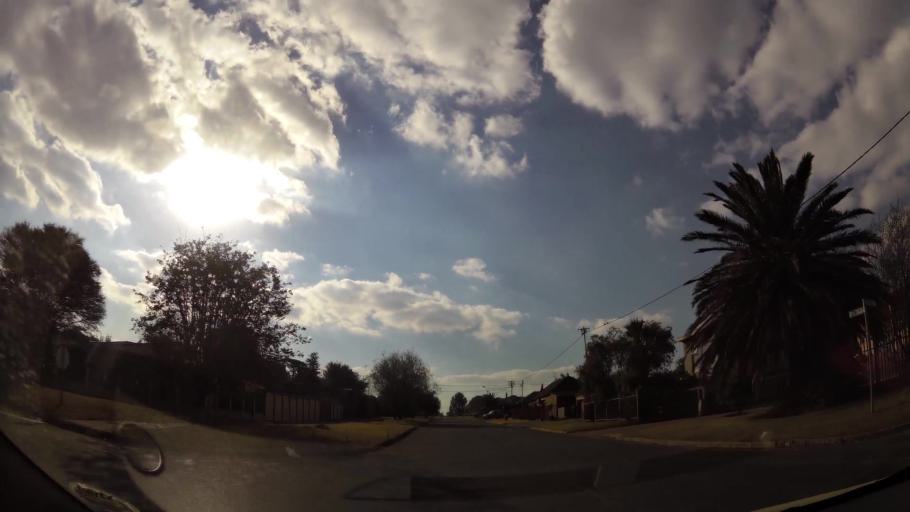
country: ZA
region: Gauteng
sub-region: West Rand District Municipality
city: Krugersdorp
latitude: -26.0924
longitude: 27.7661
